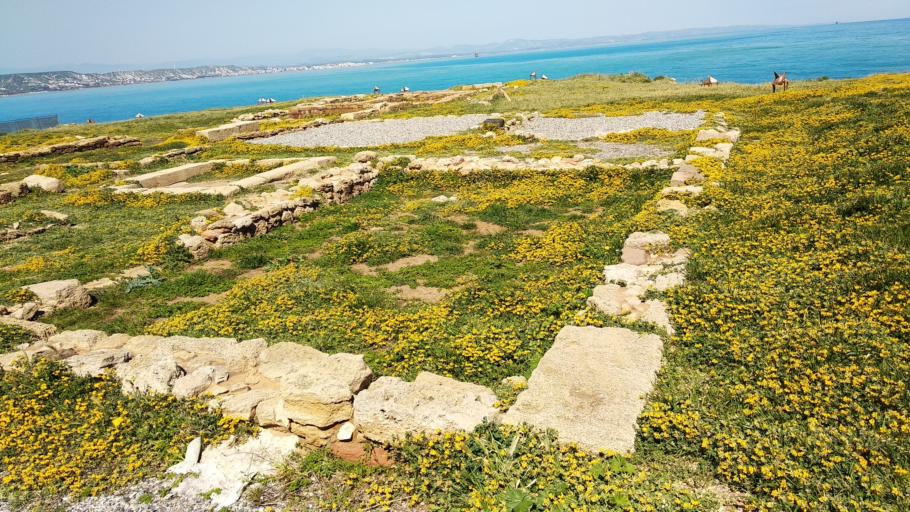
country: IT
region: Calabria
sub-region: Provincia di Crotone
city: Crotone
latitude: 39.0289
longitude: 17.2054
